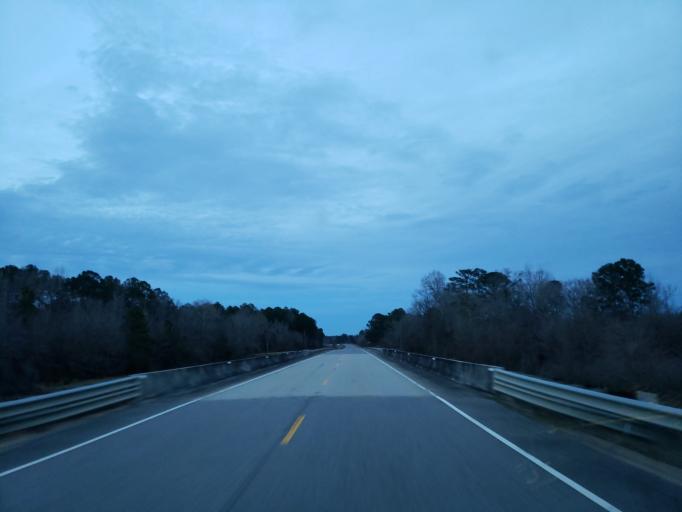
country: US
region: Alabama
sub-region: Greene County
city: Eutaw
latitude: 32.8421
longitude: -88.1312
